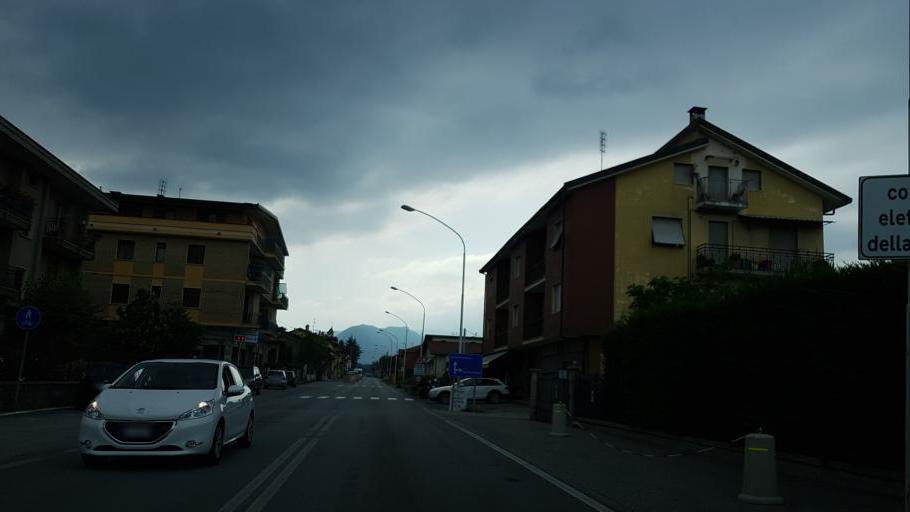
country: IT
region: Piedmont
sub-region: Provincia di Cuneo
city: Roccasparvera
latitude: 44.3347
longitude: 7.4597
